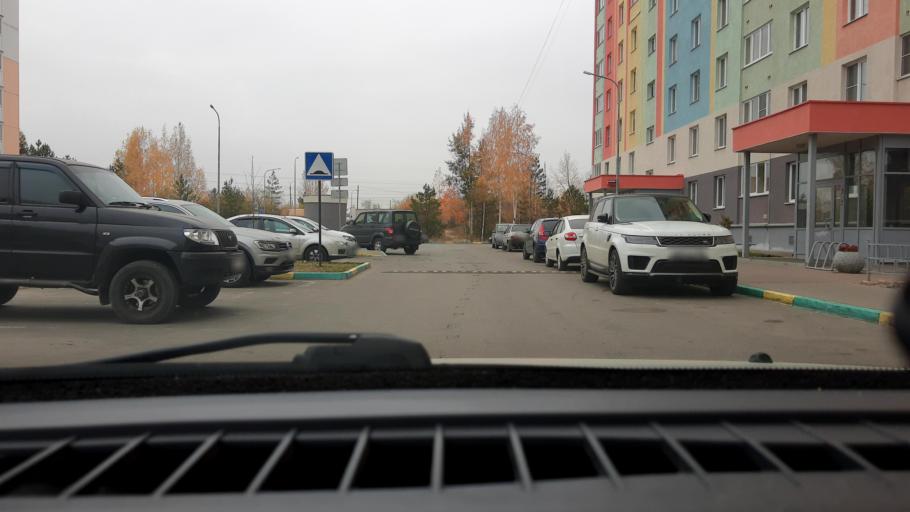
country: RU
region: Nizjnij Novgorod
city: Gorbatovka
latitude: 56.3617
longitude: 43.7978
